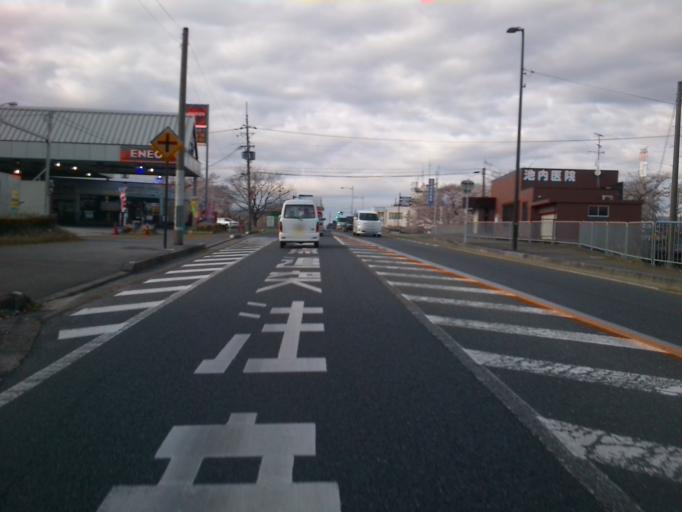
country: JP
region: Kyoto
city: Tanabe
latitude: 34.7971
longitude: 135.8031
